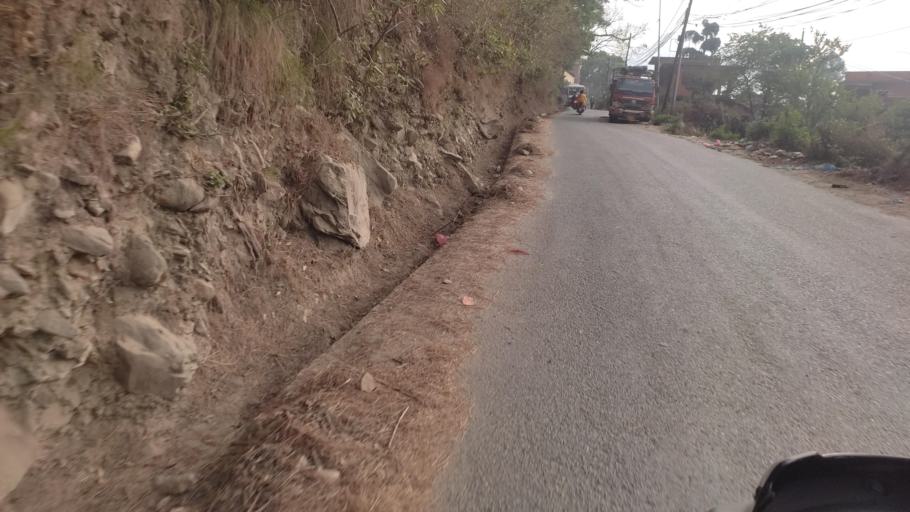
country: NP
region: Central Region
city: Kirtipur
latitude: 27.6704
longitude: 85.2885
